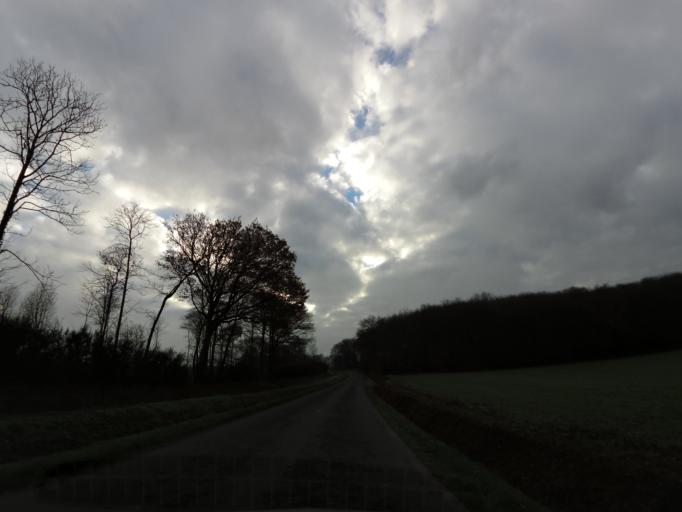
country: FR
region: Brittany
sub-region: Departement d'Ille-et-Vilaine
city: Orgeres
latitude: 47.9904
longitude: -1.6611
